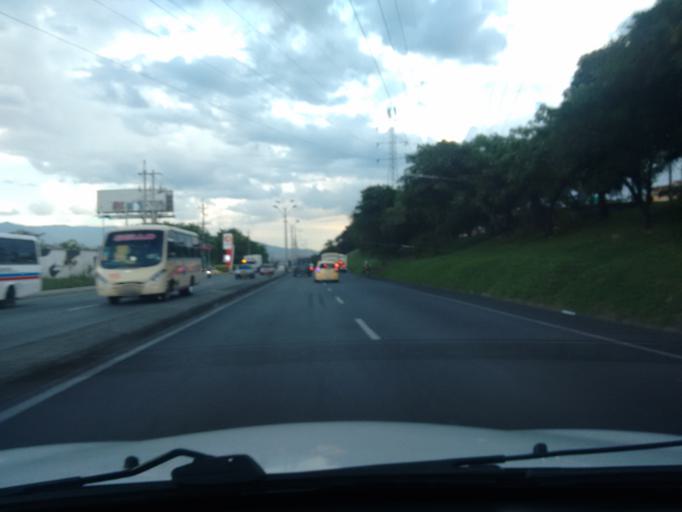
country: CO
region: Antioquia
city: Medellin
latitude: 6.2851
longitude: -75.5706
